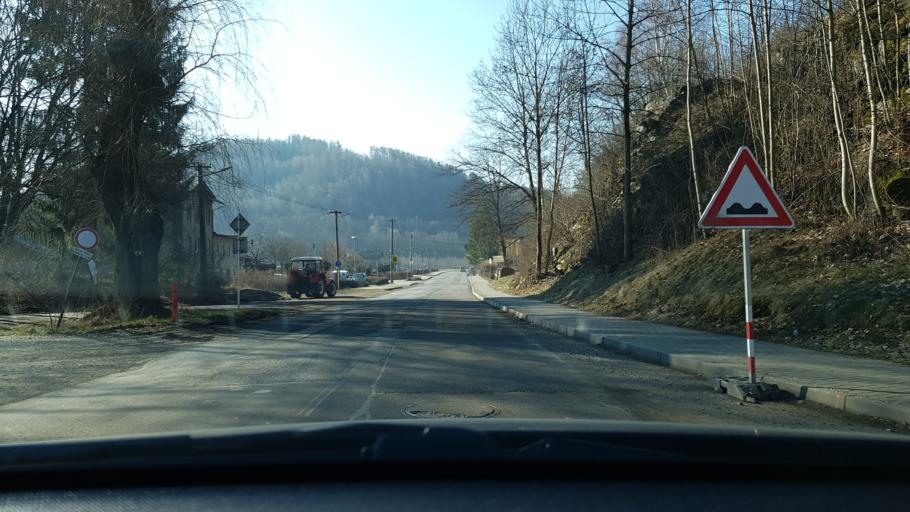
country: CZ
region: Olomoucky
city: Ruda nad Moravou
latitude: 49.9847
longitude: 16.8885
